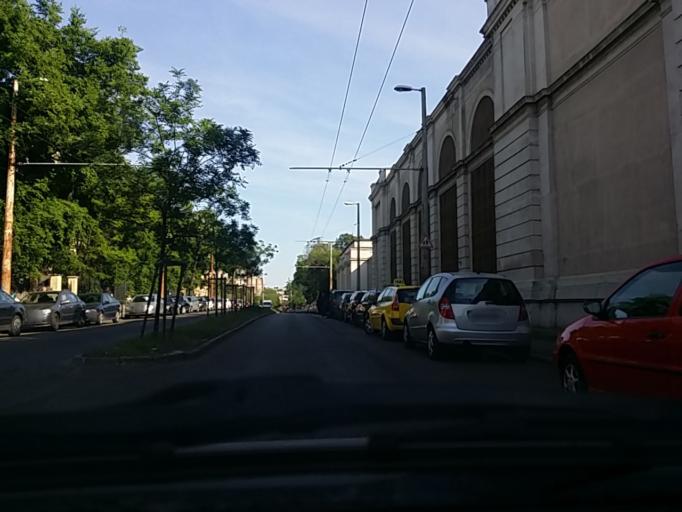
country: HU
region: Budapest
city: Budapest XIV. keruelet
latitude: 47.5145
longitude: 19.0915
